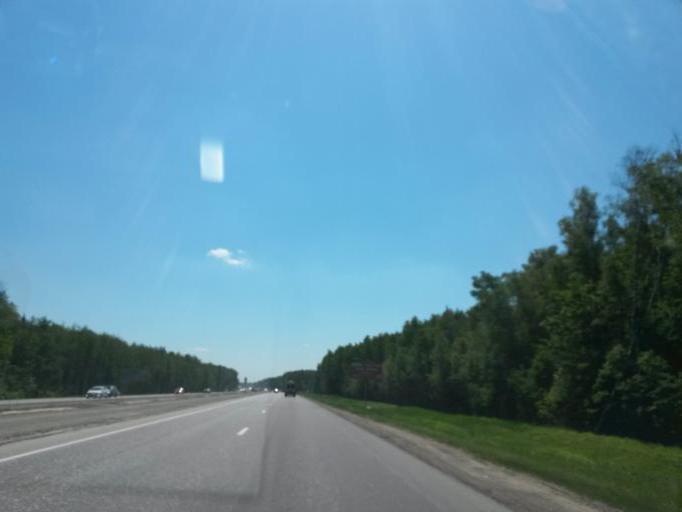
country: RU
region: Moskovskaya
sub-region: Chekhovskiy Rayon
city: Chekhov
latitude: 55.1621
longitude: 37.5437
